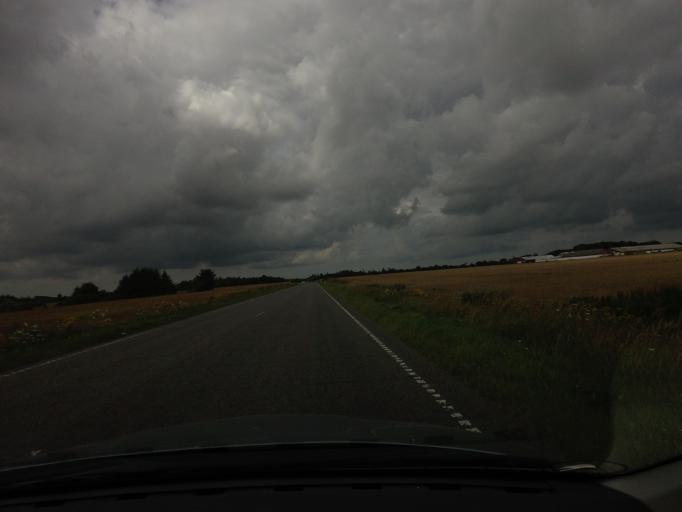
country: DK
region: North Denmark
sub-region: Hjorring Kommune
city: Hjorring
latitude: 57.4235
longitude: 10.0062
